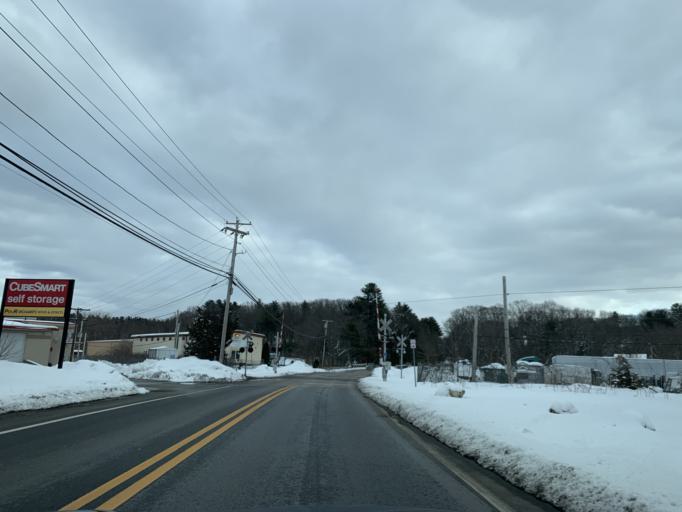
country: US
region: Massachusetts
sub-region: Norfolk County
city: Franklin
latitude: 42.0881
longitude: -71.4282
